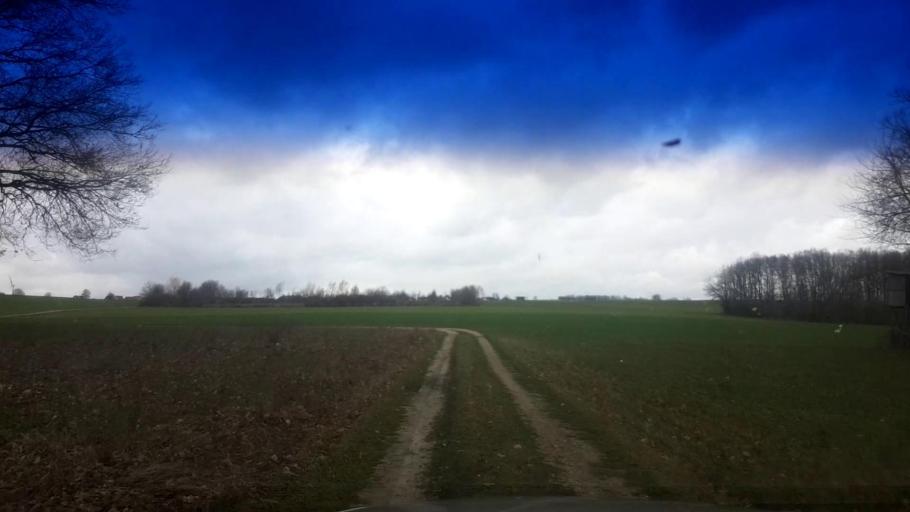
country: DE
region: Bavaria
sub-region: Upper Franconia
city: Zapfendorf
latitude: 49.9797
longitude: 10.9557
